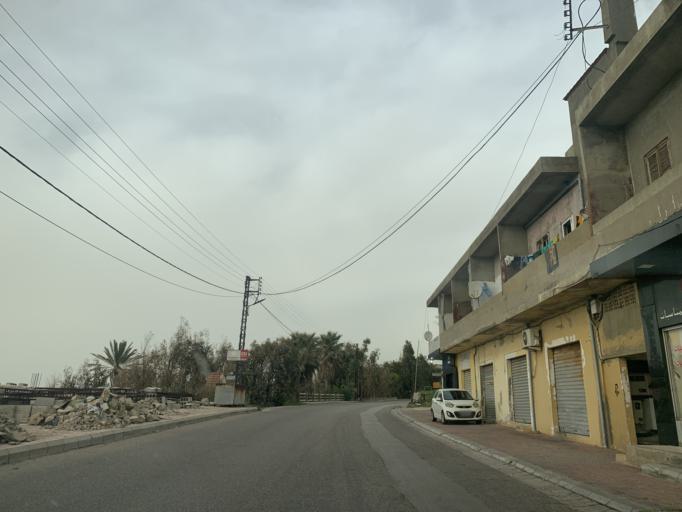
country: LB
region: Mont-Liban
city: Jbail
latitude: 34.0843
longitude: 35.6494
